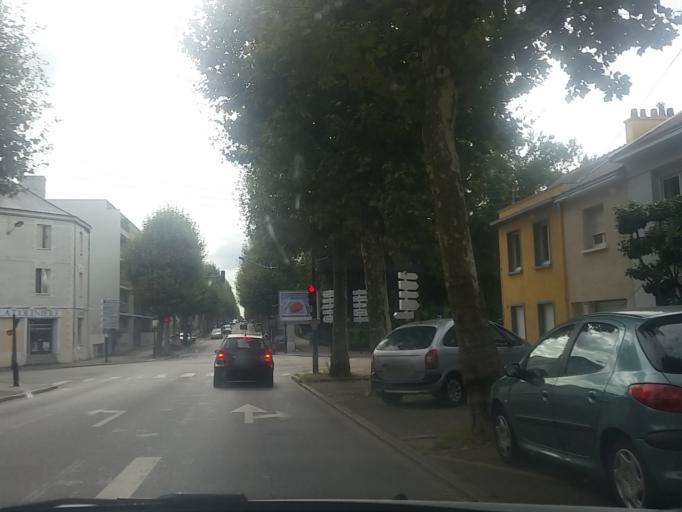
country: FR
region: Pays de la Loire
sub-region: Departement de la Loire-Atlantique
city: Nantes
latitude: 47.2288
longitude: -1.5269
